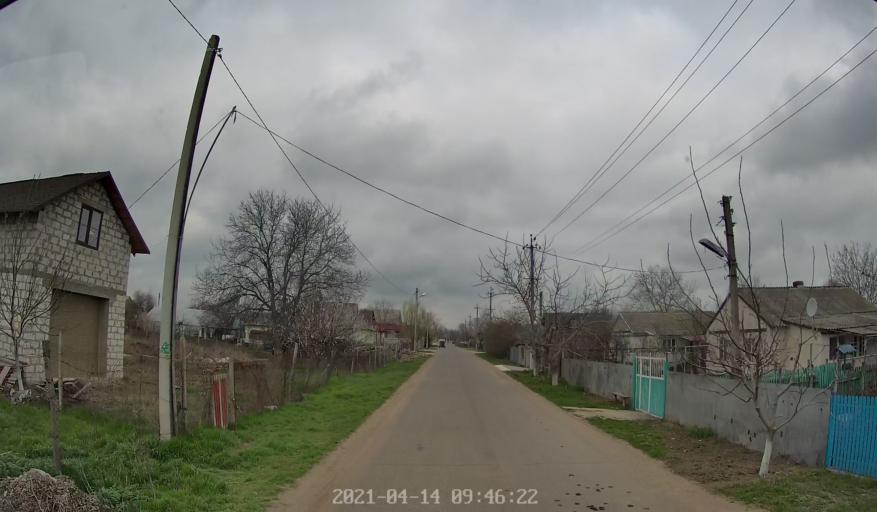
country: MD
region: Chisinau
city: Vadul lui Voda
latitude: 47.1346
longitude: 29.1230
